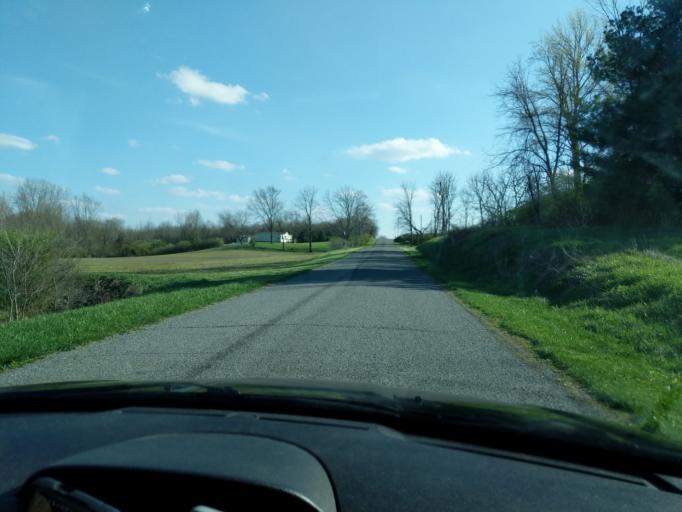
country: US
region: Ohio
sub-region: Champaign County
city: Urbana
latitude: 40.1645
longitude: -83.8324
